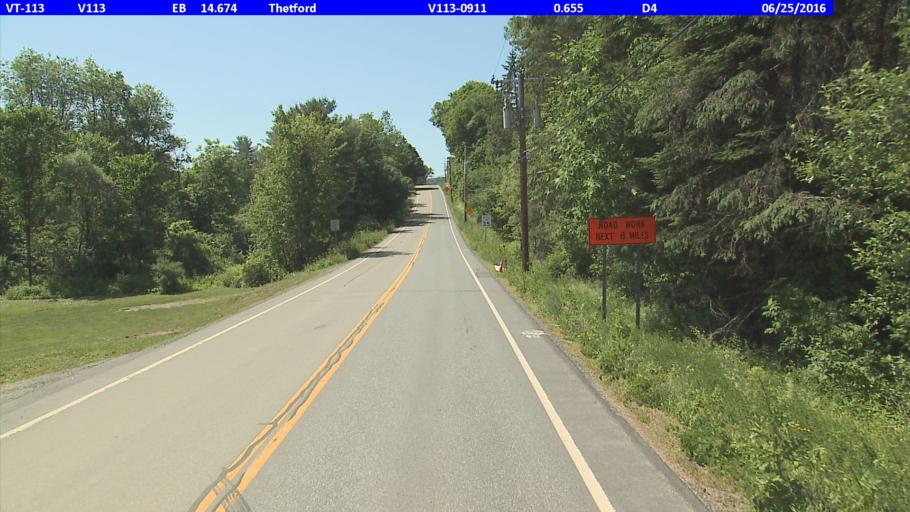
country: US
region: New Hampshire
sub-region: Grafton County
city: Orford
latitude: 43.8885
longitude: -72.2597
